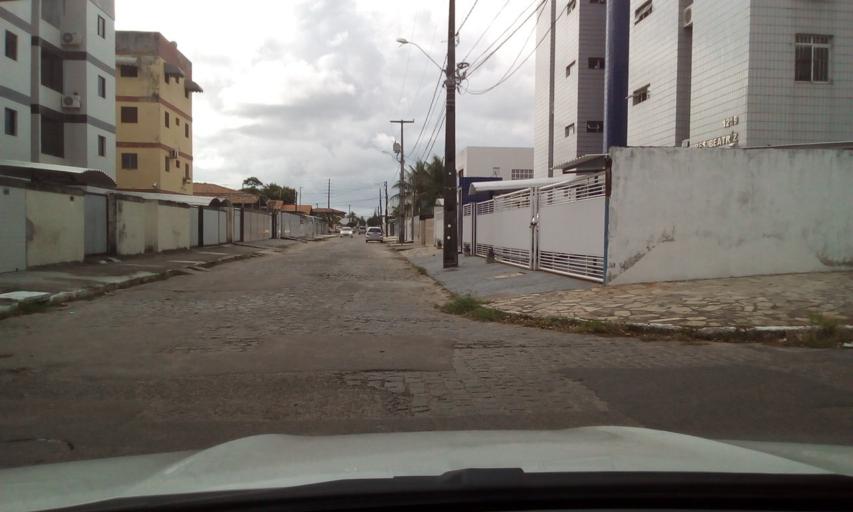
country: BR
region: Paraiba
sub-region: Joao Pessoa
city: Joao Pessoa
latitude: -7.1587
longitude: -34.8757
